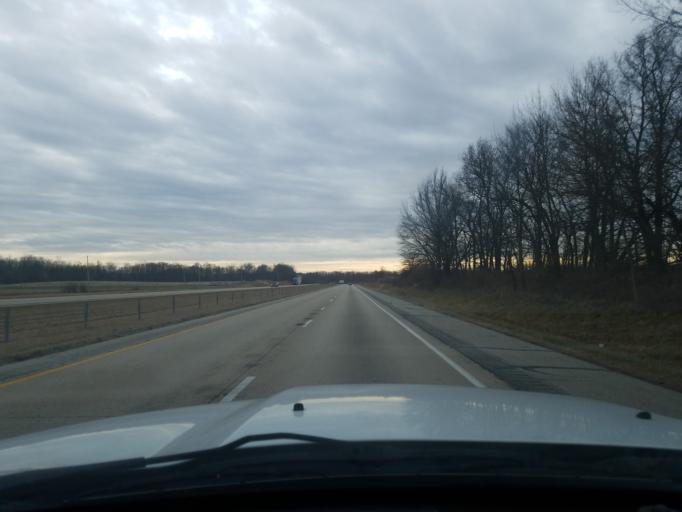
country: US
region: Indiana
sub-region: Grant County
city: Upland
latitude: 40.4655
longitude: -85.5509
